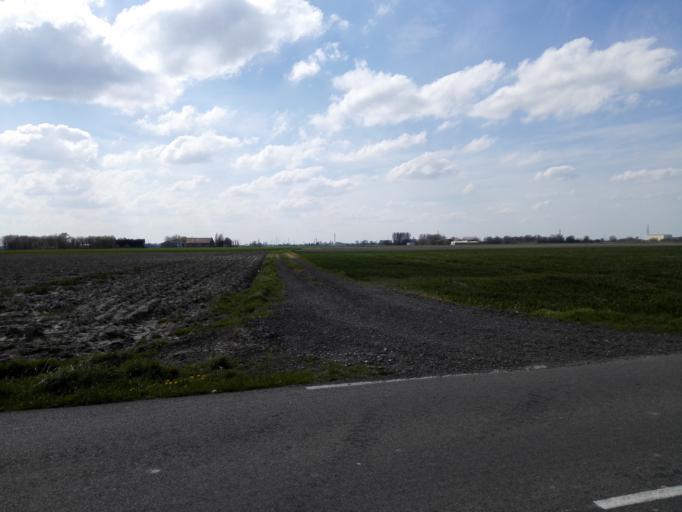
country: FR
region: Nord-Pas-de-Calais
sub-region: Departement du Nord
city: Spycker
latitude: 50.9758
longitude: 2.3103
